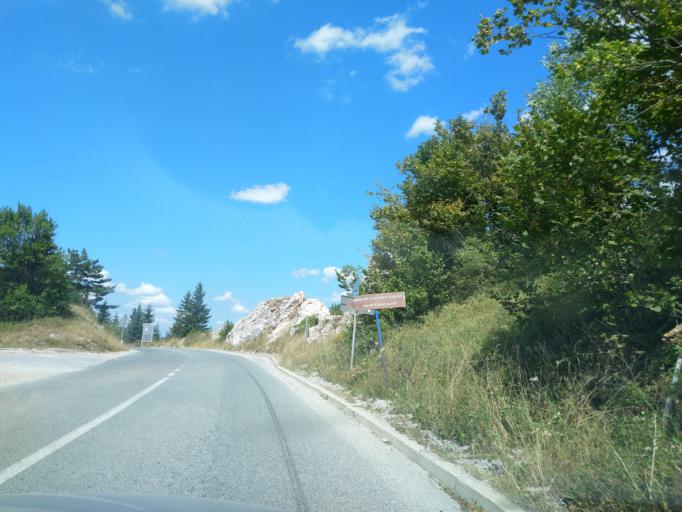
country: RS
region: Central Serbia
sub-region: Zlatiborski Okrug
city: Nova Varos
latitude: 43.4044
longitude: 19.8440
